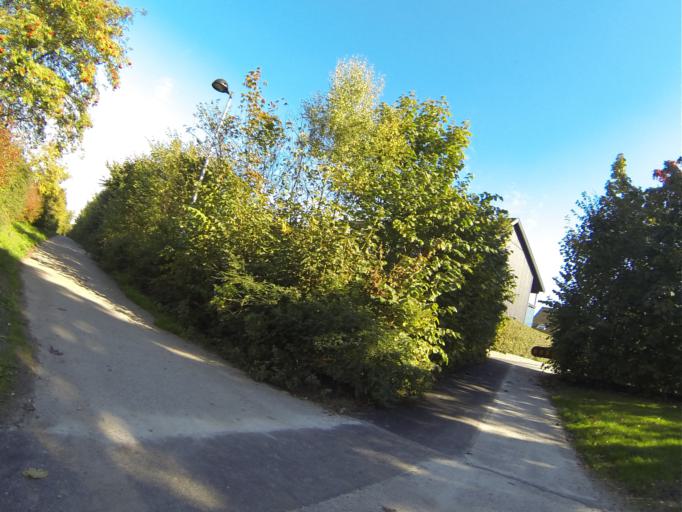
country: SE
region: Skane
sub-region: Lunds Kommun
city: Genarp
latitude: 55.7081
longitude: 13.3310
